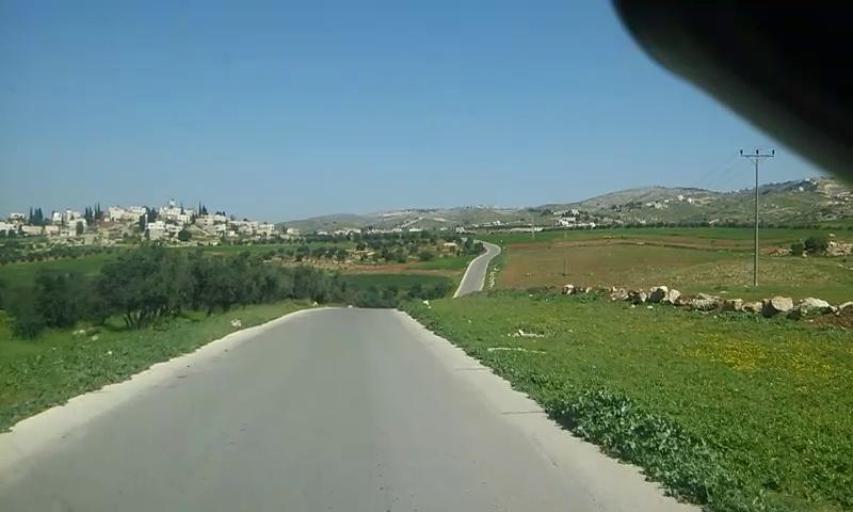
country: PS
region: West Bank
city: Dayr al `Asal al Fawqa
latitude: 31.4681
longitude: 34.9426
